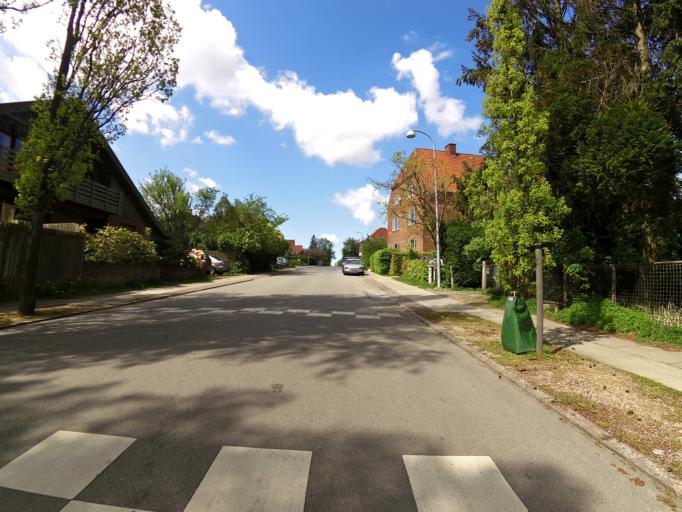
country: DK
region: Capital Region
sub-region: Gladsaxe Municipality
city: Buddinge
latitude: 55.7326
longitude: 12.5076
